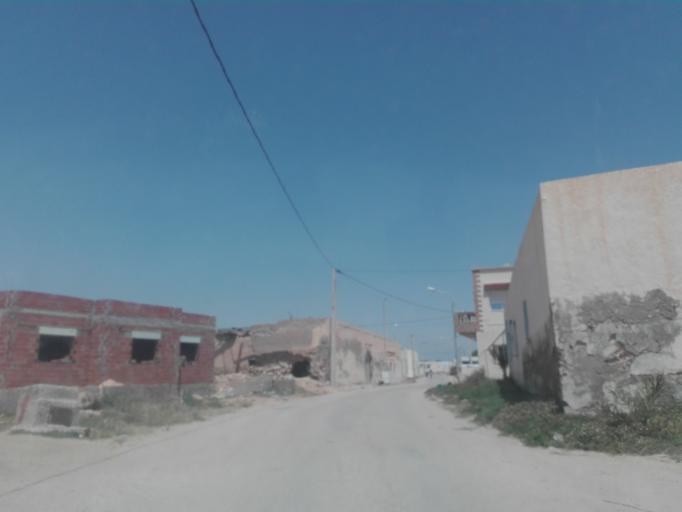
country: TN
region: Safaqis
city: Al Qarmadah
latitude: 34.6523
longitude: 11.0309
